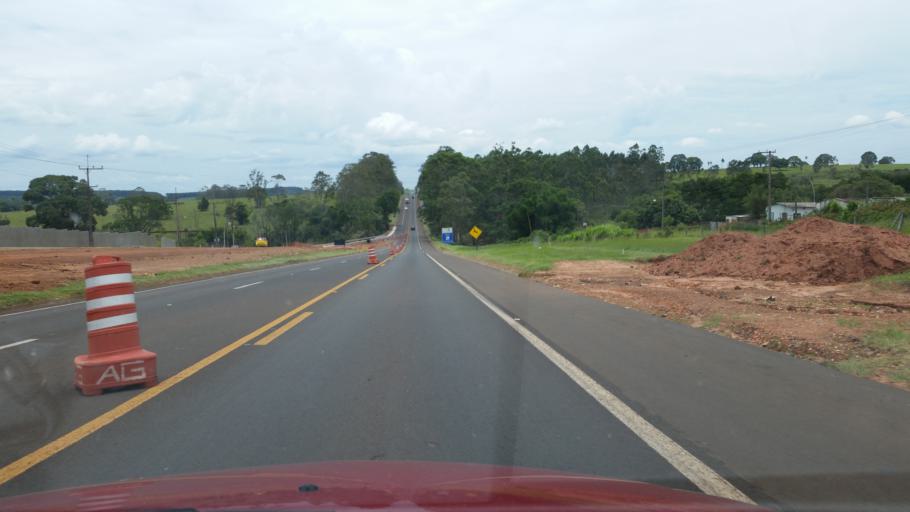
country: BR
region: Sao Paulo
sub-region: Avare
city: Avare
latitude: -23.0725
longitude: -48.9218
